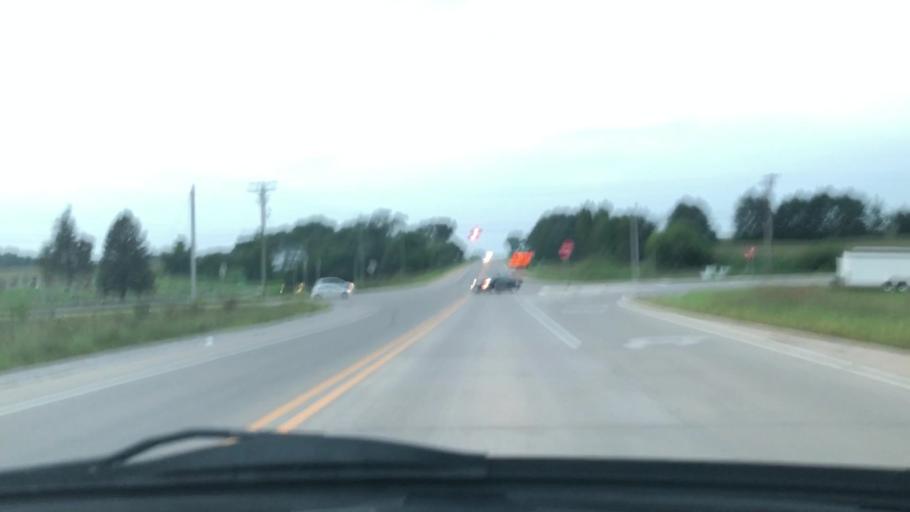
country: US
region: Iowa
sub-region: Linn County
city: Ely
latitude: 41.8472
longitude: -91.6754
